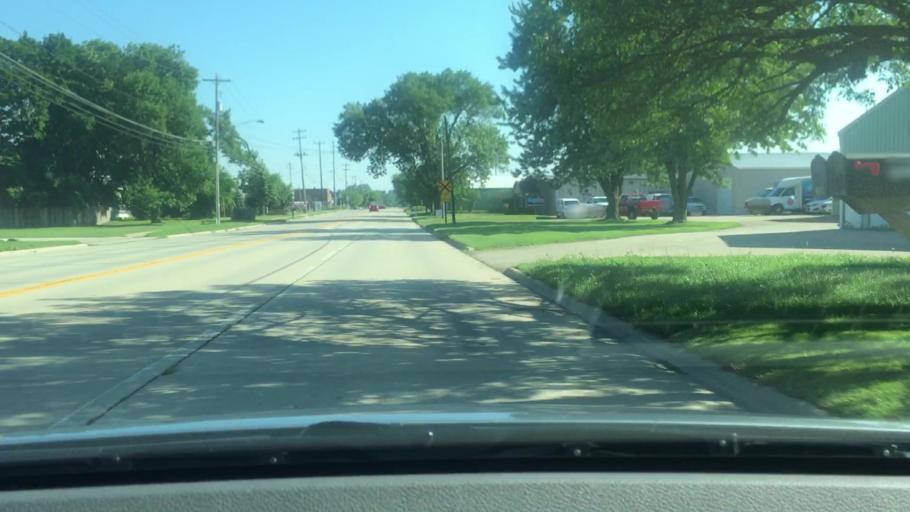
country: US
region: Wisconsin
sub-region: Winnebago County
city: Oshkosh
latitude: 43.9885
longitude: -88.5426
